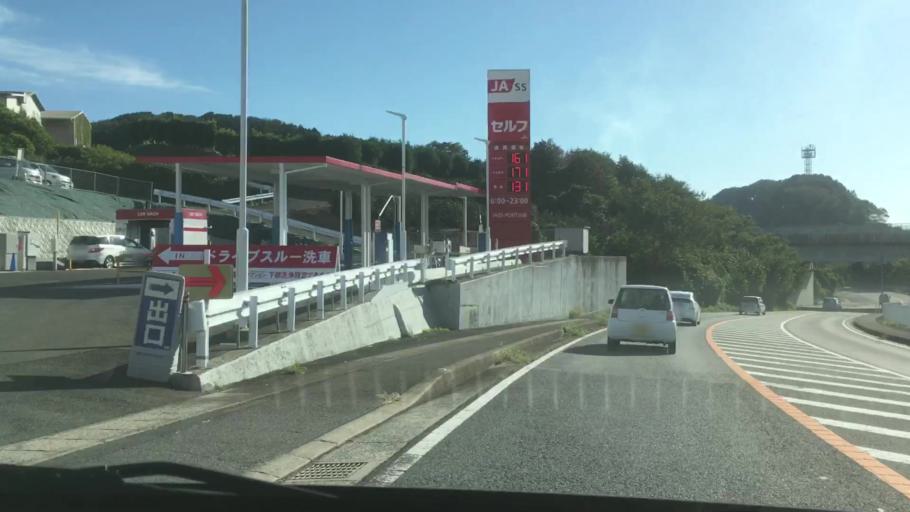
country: JP
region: Nagasaki
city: Sasebo
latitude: 33.0470
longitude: 129.7491
